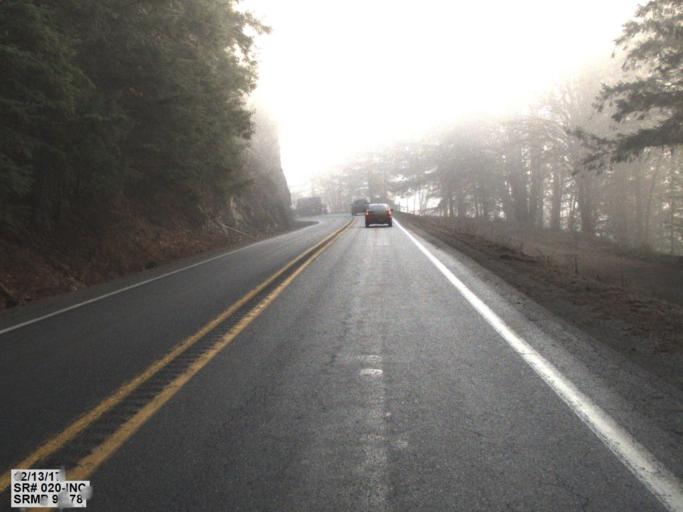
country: US
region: Washington
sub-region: Snohomish County
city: Darrington
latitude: 48.4917
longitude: -121.5680
